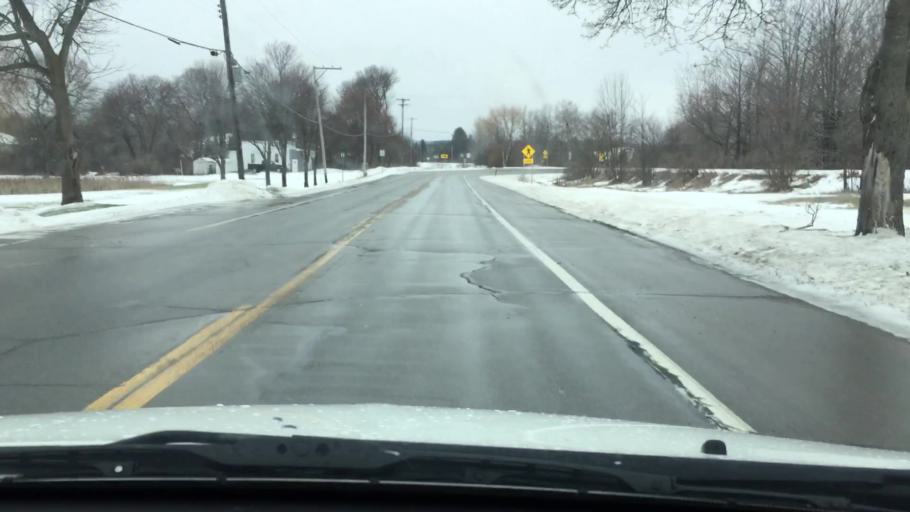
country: US
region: Michigan
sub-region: Wexford County
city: Cadillac
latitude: 44.2350
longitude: -85.4131
